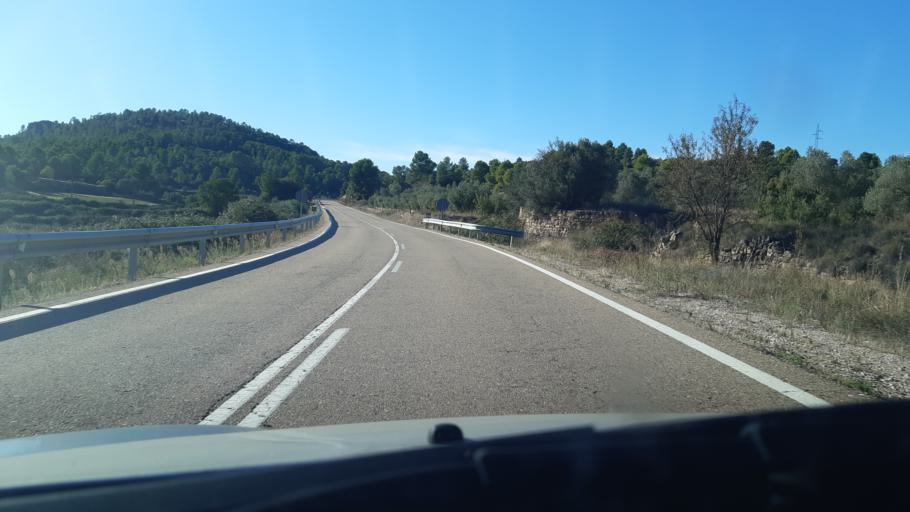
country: ES
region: Aragon
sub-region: Provincia de Teruel
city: Valjunquera
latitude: 40.9432
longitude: 0.0608
